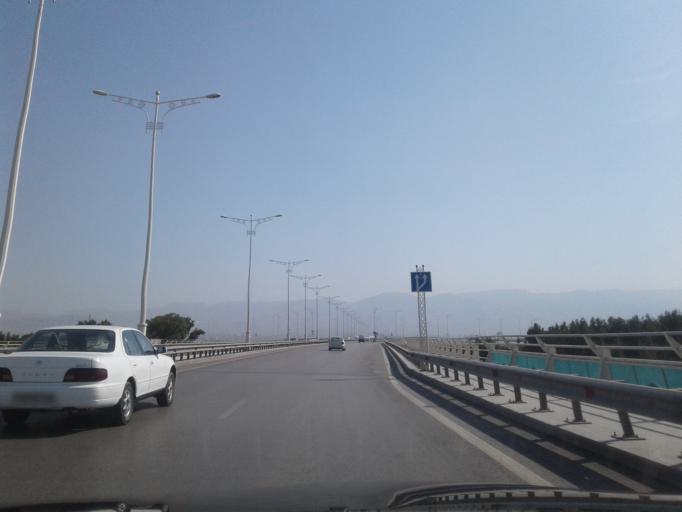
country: TM
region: Ahal
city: Ashgabat
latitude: 37.9640
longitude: 58.4215
